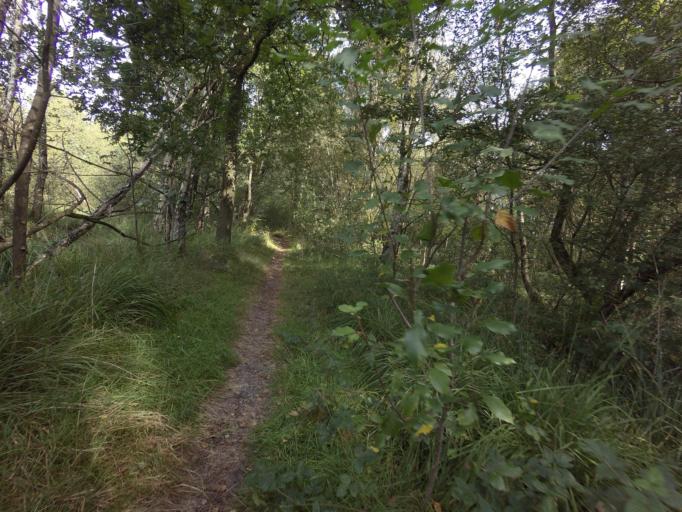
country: DE
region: North Rhine-Westphalia
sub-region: Regierungsbezirk Munster
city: Gronau
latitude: 52.1854
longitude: 6.9605
